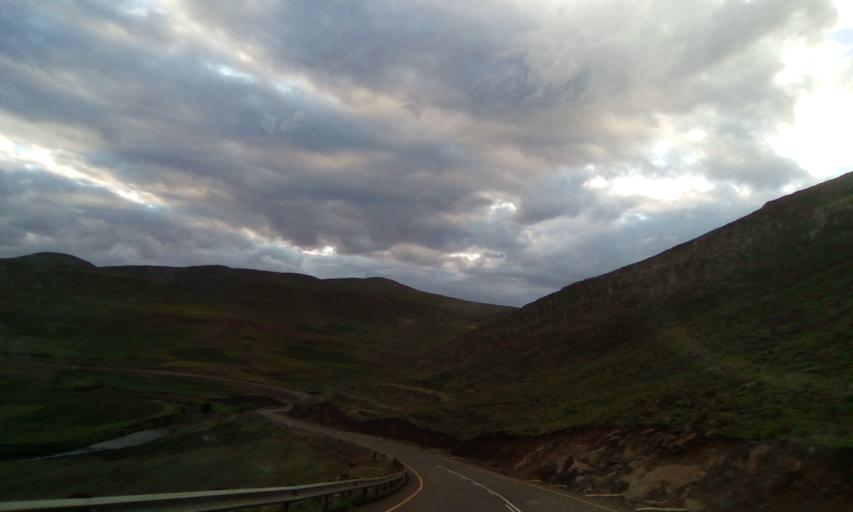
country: LS
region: Maseru
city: Nako
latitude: -29.8031
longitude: 28.0320
